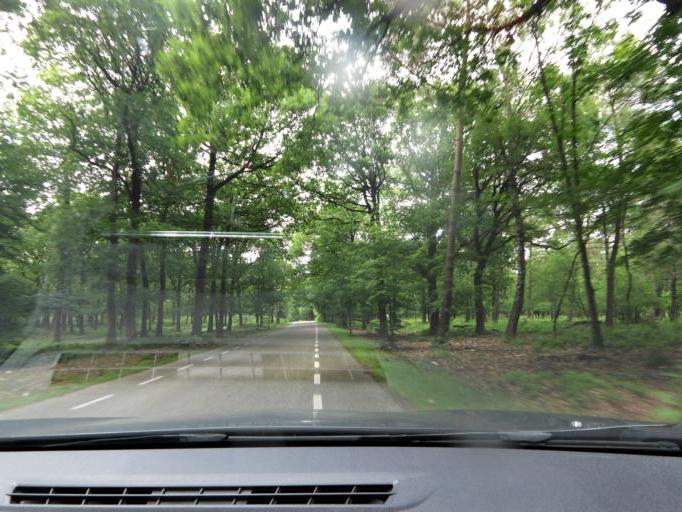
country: NL
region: Gelderland
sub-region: Gemeente Apeldoorn
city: Uddel
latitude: 52.2453
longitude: 5.8235
